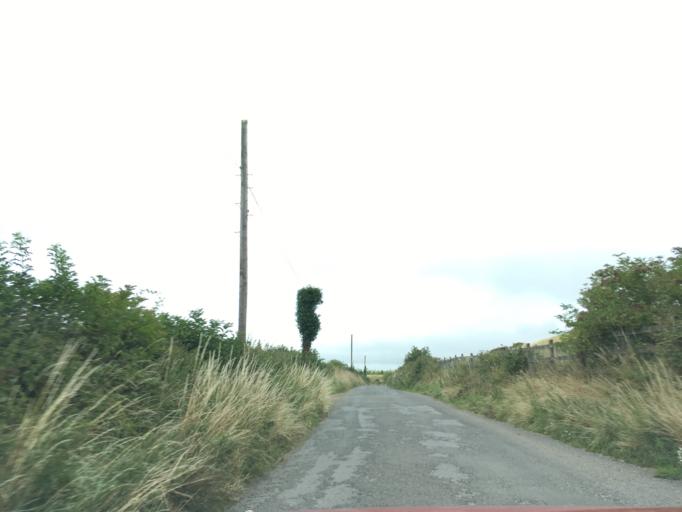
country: IE
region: Munster
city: Cashel
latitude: 52.4769
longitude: -7.9085
